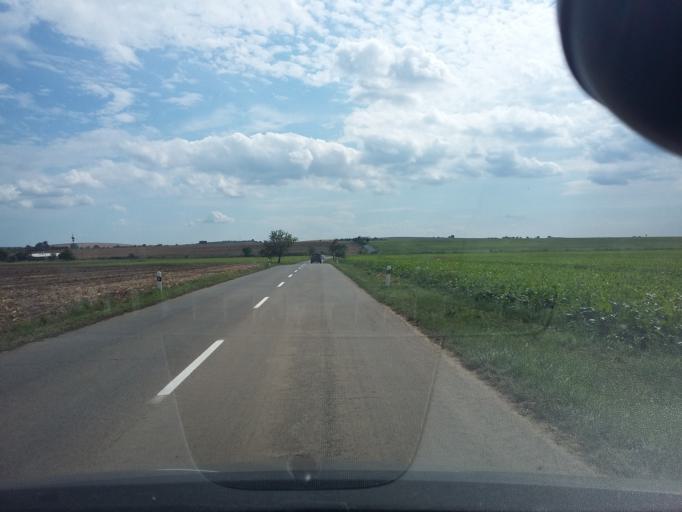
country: SK
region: Trnavsky
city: Gbely
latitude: 48.7378
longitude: 17.1677
